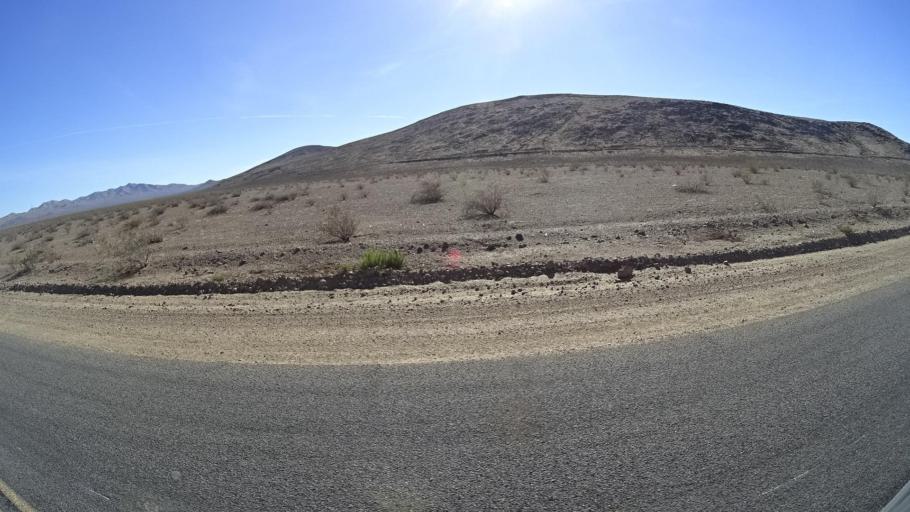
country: US
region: California
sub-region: Kern County
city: China Lake Acres
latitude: 35.5607
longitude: -117.7675
